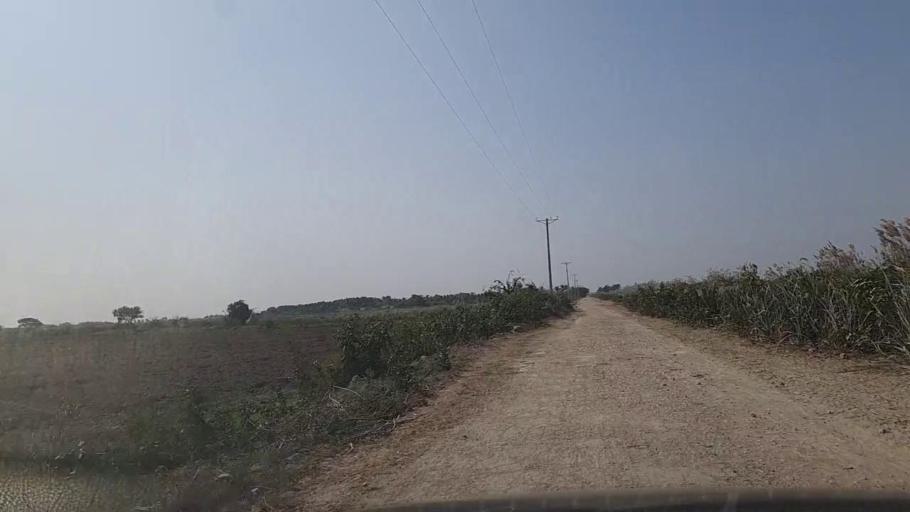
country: PK
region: Sindh
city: Gharo
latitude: 24.6819
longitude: 67.5983
